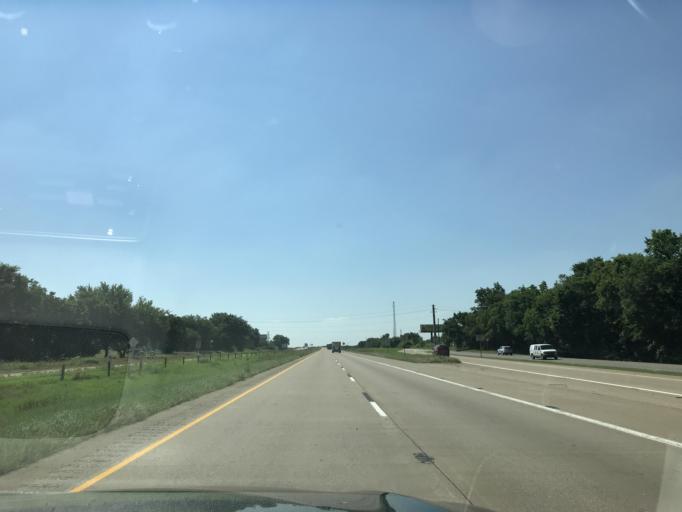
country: US
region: Texas
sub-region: Johnson County
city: Alvarado
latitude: 32.3982
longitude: -97.2175
